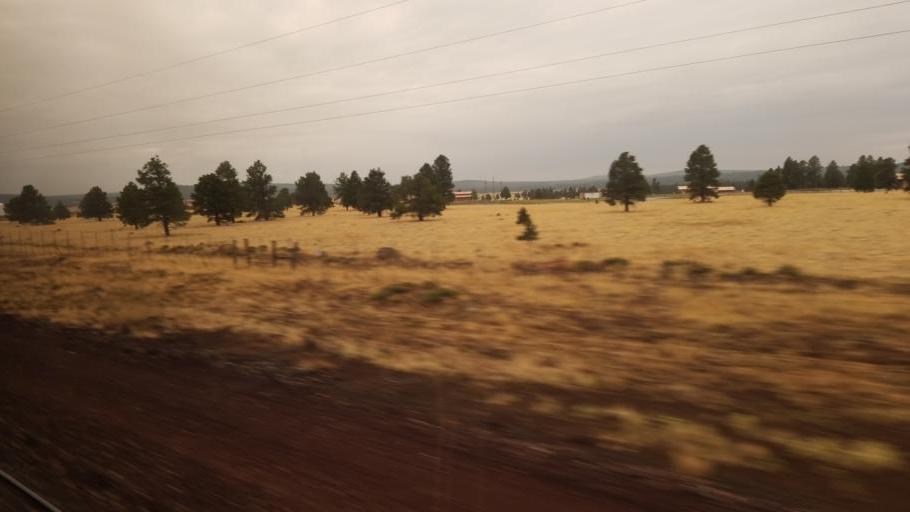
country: US
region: Arizona
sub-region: Coconino County
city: Parks
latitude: 35.2402
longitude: -111.8491
